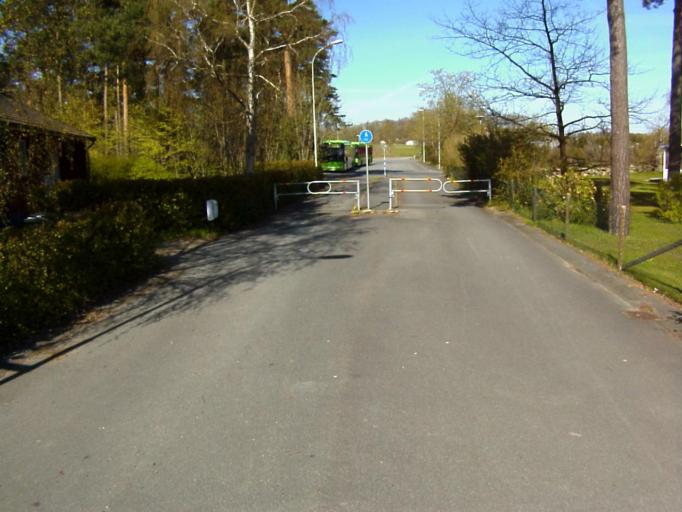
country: SE
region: Skane
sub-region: Kristianstads Kommun
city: Norra Asum
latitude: 55.9997
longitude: 14.0815
